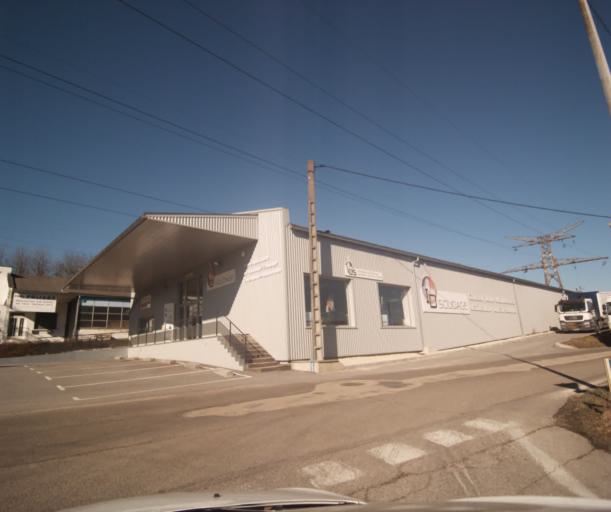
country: FR
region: Franche-Comte
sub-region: Departement du Doubs
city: Thise
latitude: 47.2653
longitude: 6.0551
